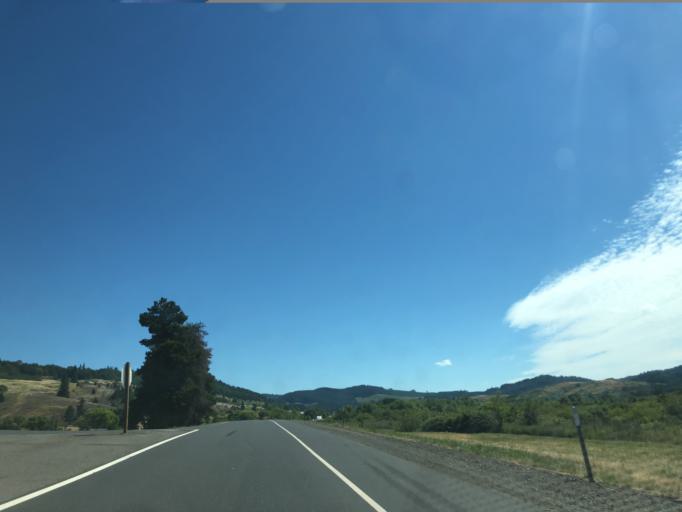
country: US
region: Oregon
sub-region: Douglas County
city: Yoncalla
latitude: 43.5649
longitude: -123.2810
